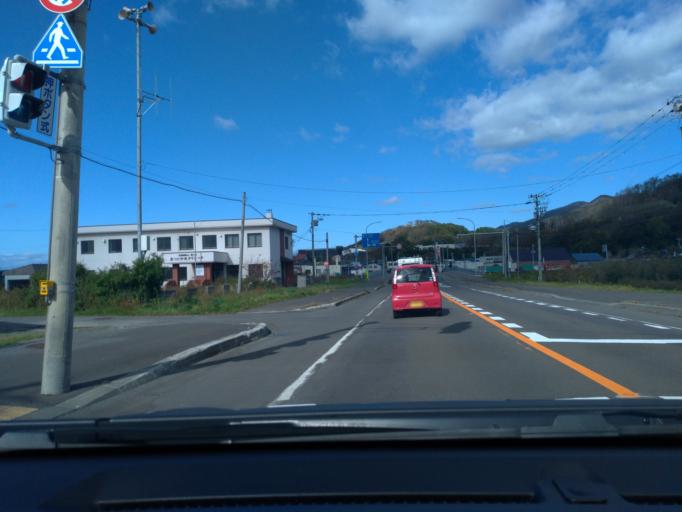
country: JP
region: Hokkaido
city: Ishikari
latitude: 43.3975
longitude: 141.4369
